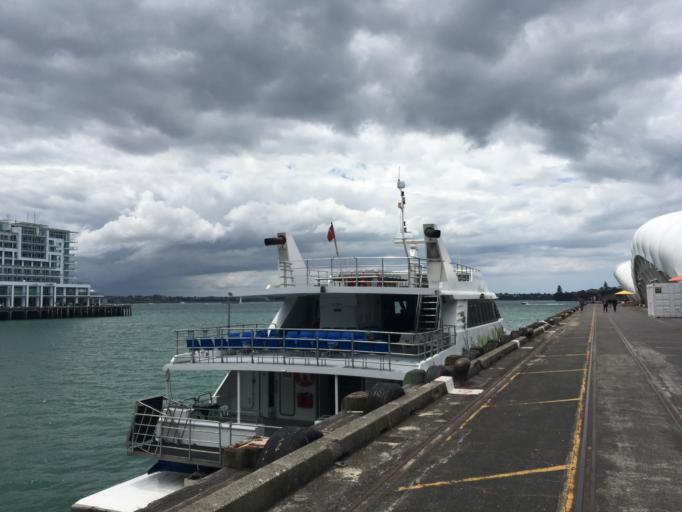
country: NZ
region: Auckland
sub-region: Auckland
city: Auckland
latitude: -36.8416
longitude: 174.7675
